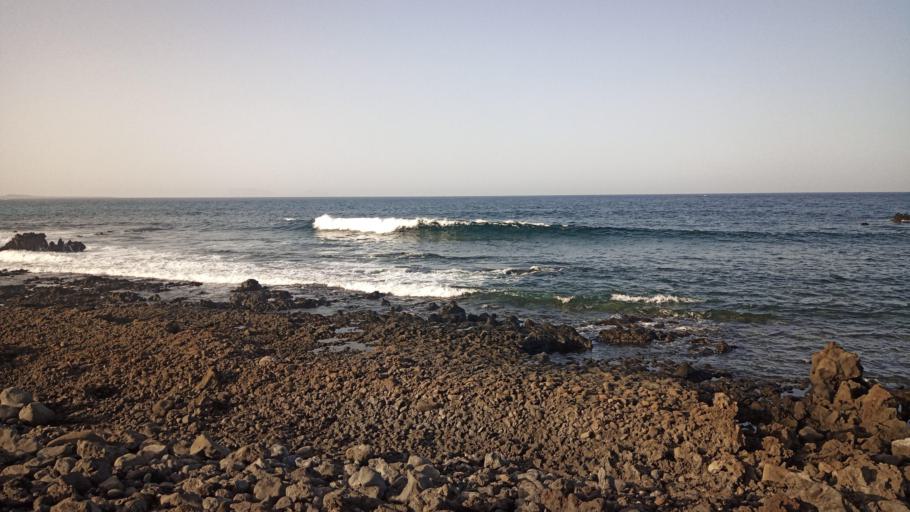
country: ES
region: Canary Islands
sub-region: Provincia de Las Palmas
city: Haria
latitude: 29.2085
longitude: -13.4254
